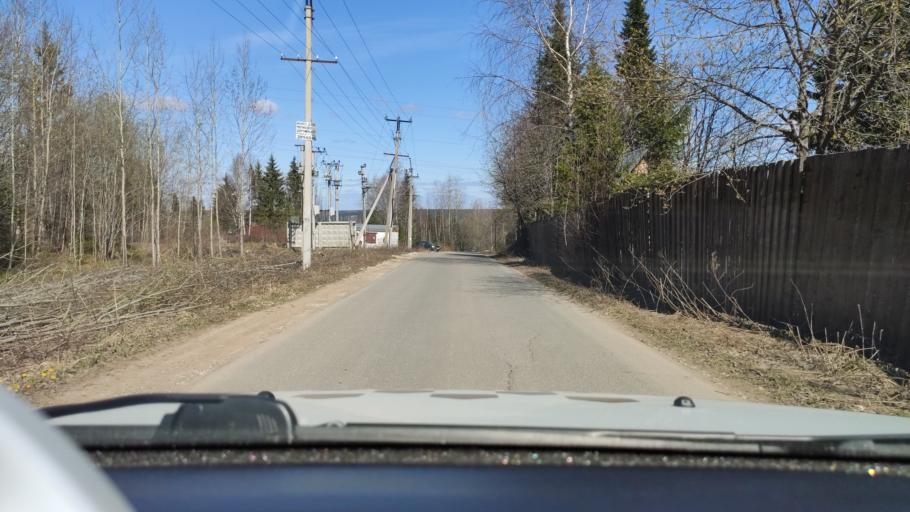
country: RU
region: Perm
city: Novyye Lyady
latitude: 58.0482
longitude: 56.6428
